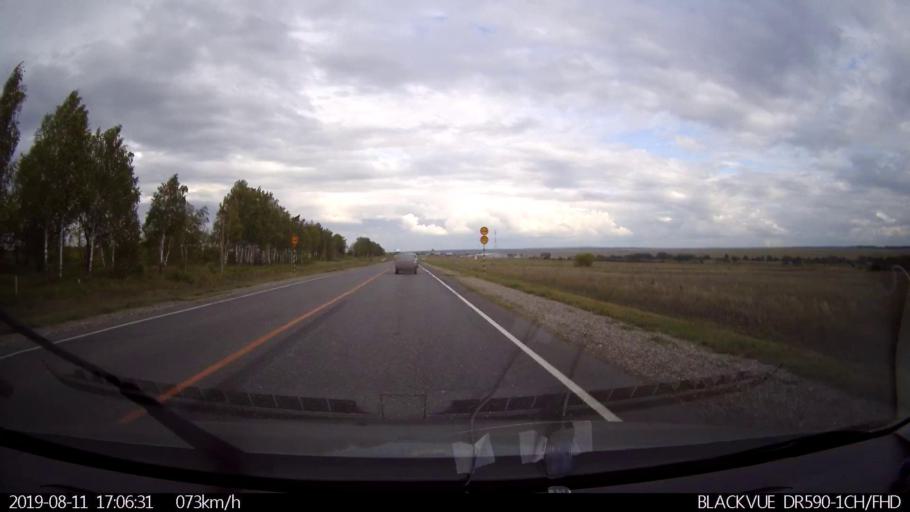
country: RU
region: Ulyanovsk
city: Mayna
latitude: 54.2952
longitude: 47.8073
